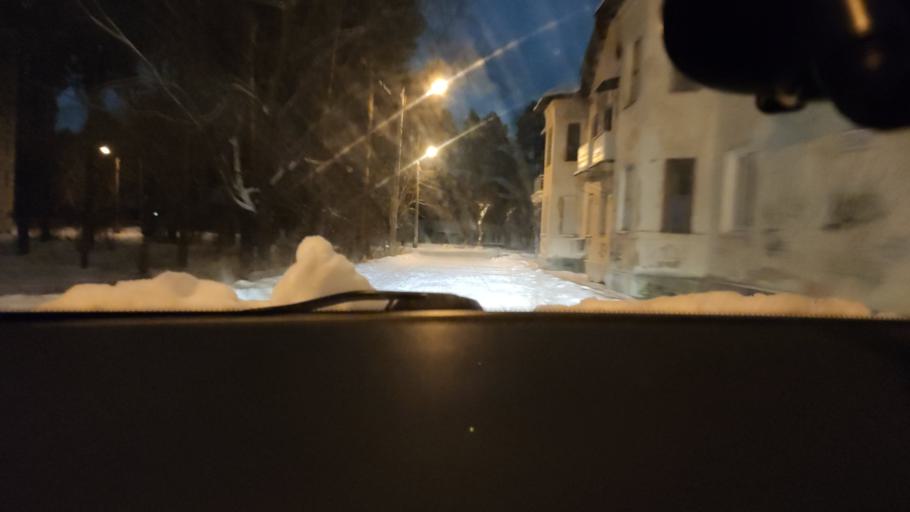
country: RU
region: Perm
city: Krasnokamsk
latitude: 58.0793
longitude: 55.7445
